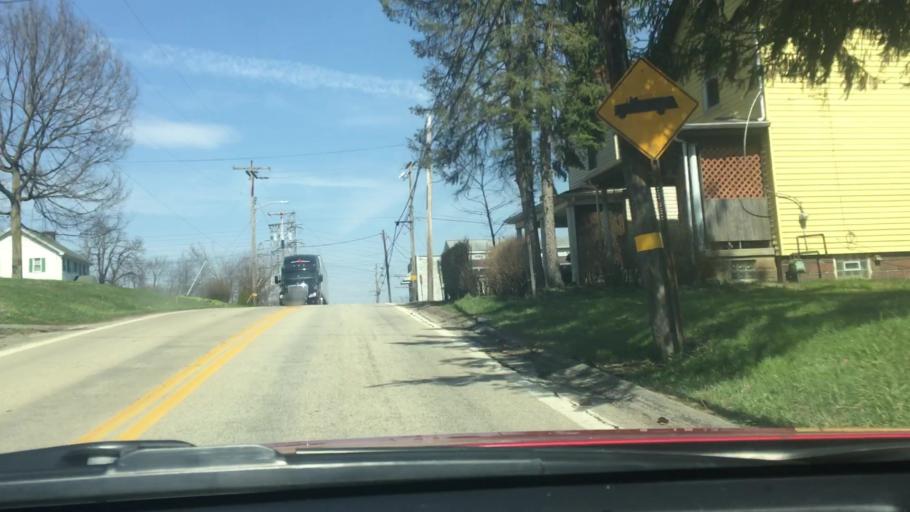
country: US
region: Pennsylvania
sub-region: Allegheny County
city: Jefferson Hills
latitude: 40.2528
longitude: -79.9270
